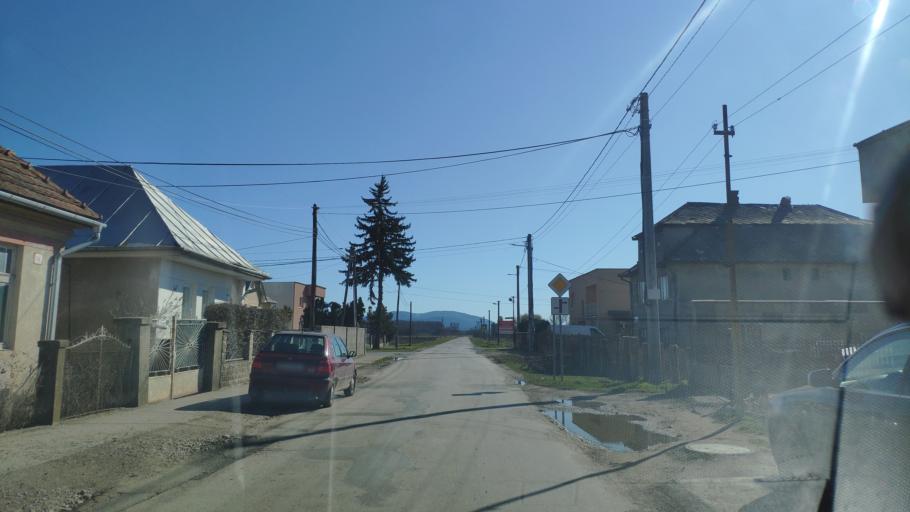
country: SK
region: Kosicky
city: Kosice
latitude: 48.6058
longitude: 21.3223
